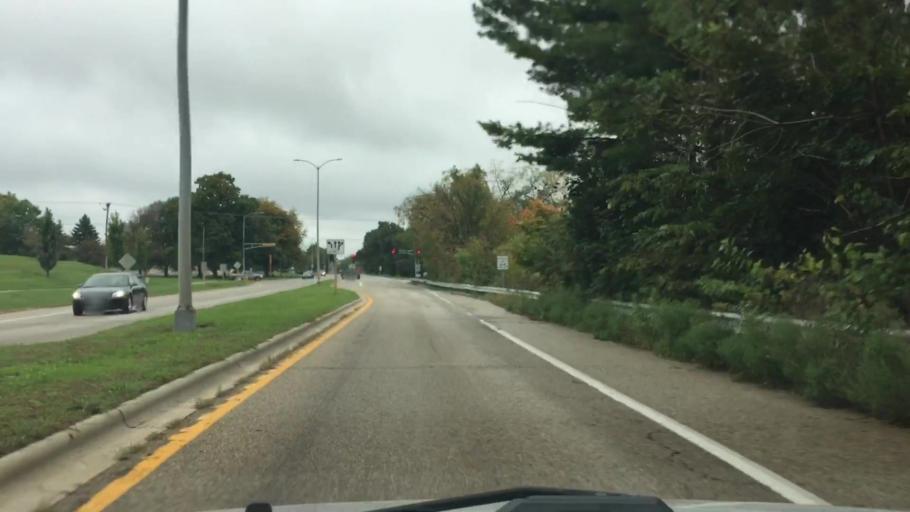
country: US
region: Wisconsin
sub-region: Rock County
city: Janesville
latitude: 42.7056
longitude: -89.0310
